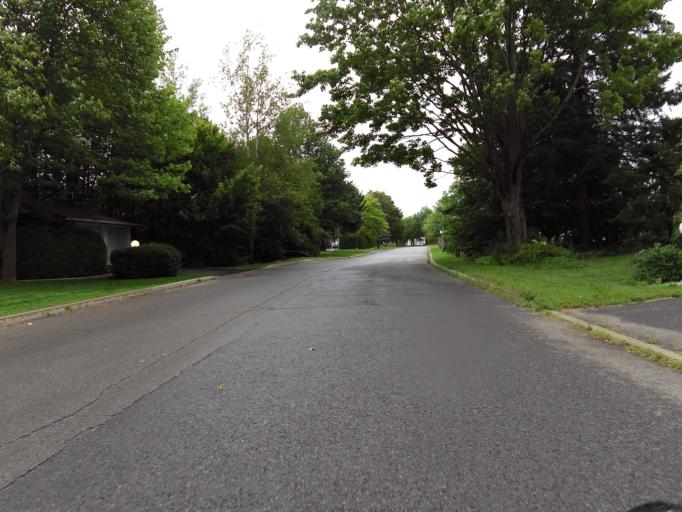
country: CA
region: Ontario
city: Bells Corners
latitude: 45.3292
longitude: -75.9050
